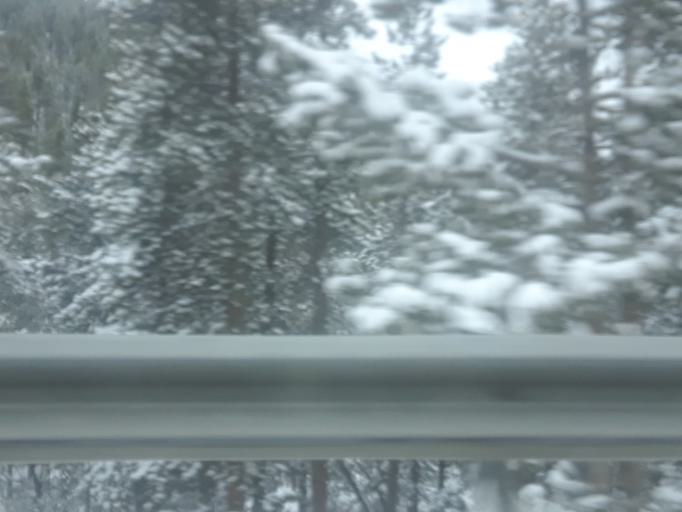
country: US
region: Colorado
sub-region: Boulder County
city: Coal Creek
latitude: 39.9259
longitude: -105.4074
